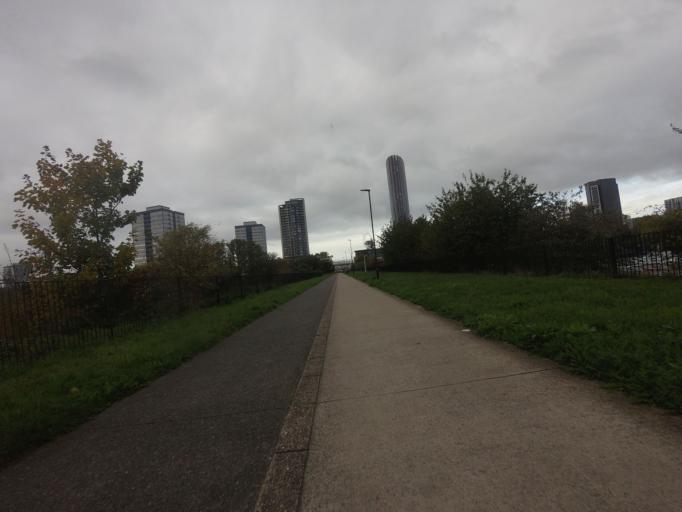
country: GB
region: England
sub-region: Greater London
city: Poplar
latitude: 51.5325
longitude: -0.0033
